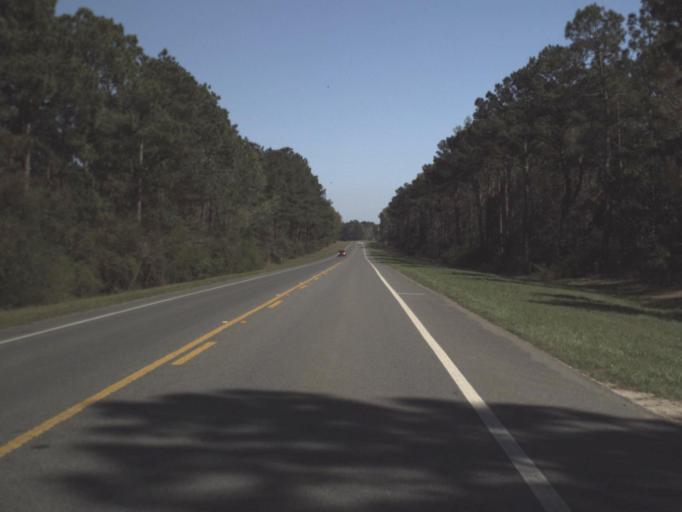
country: US
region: Florida
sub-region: Walton County
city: DeFuniak Springs
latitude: 30.7252
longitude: -85.9610
